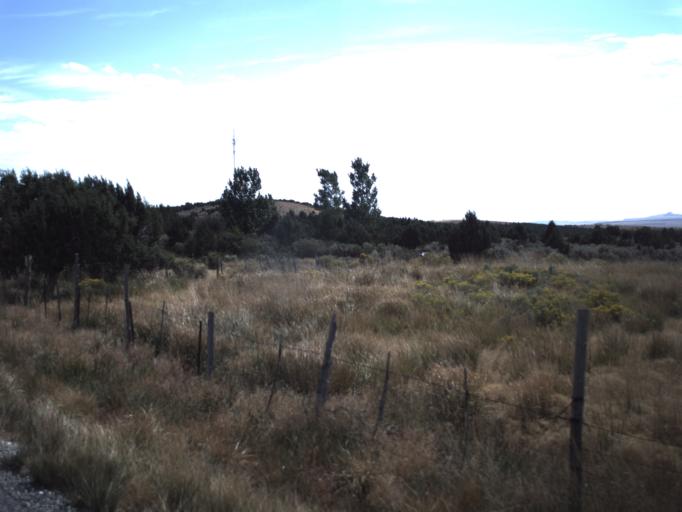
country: US
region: Idaho
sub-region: Cassia County
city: Burley
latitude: 41.8171
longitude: -113.3106
